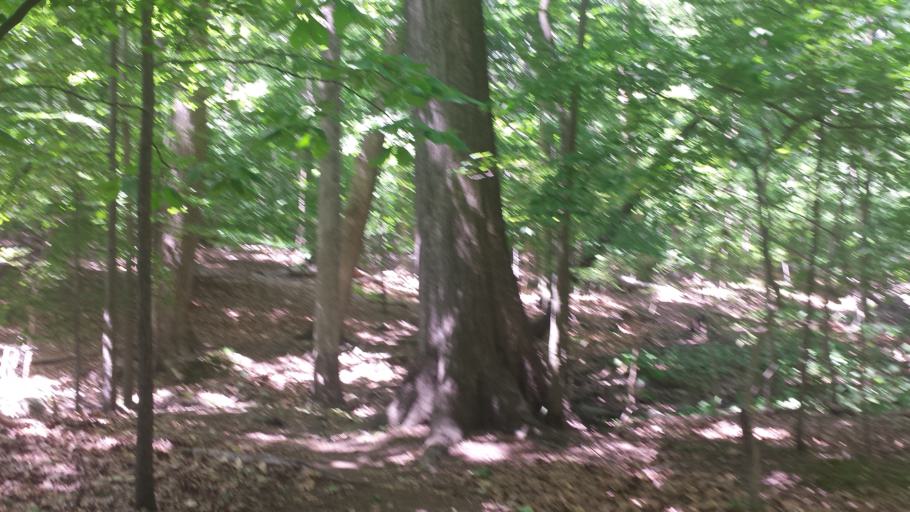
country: US
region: New York
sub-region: Westchester County
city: Harrison
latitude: 40.9540
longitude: -73.7000
